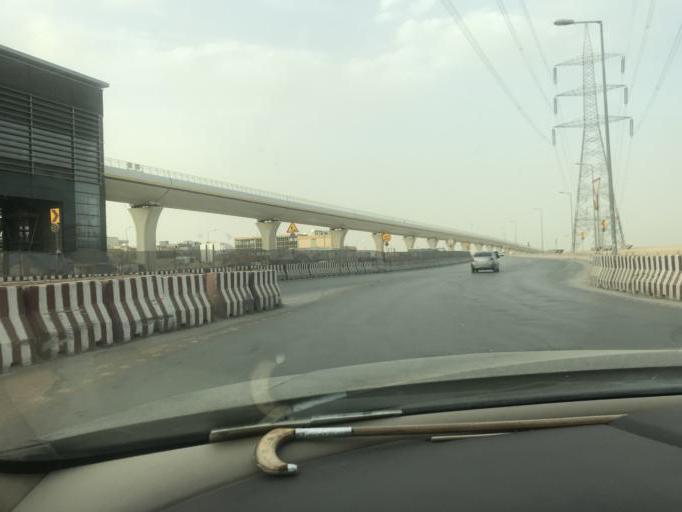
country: SA
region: Ar Riyad
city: Riyadh
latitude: 24.7859
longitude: 46.6608
